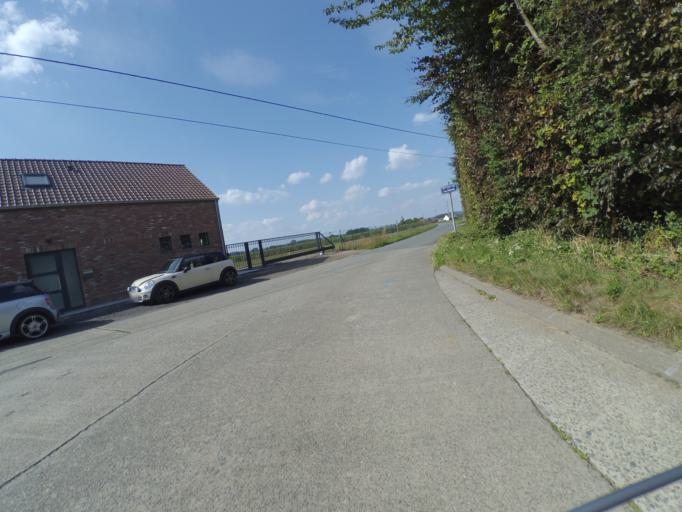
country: BE
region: Wallonia
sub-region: Province du Hainaut
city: Frasnes-lez-Buissenal
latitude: 50.6855
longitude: 3.5559
